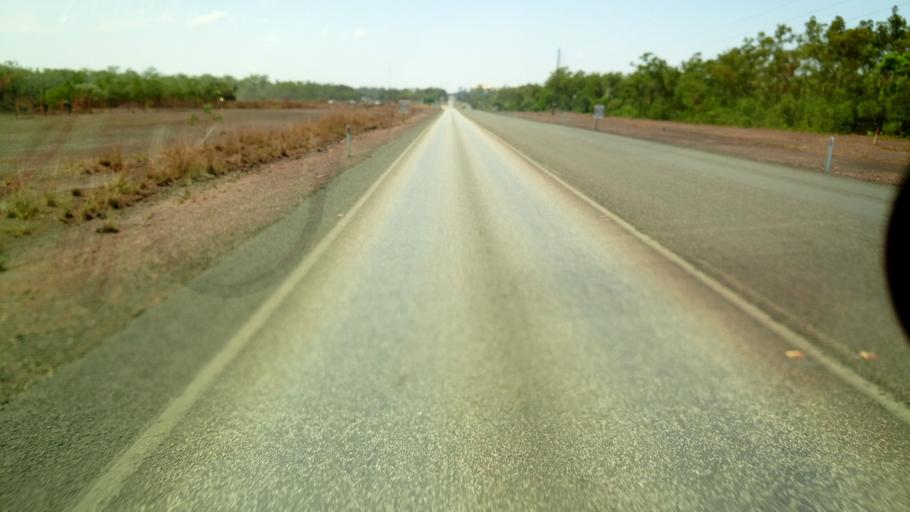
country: AU
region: Northern Territory
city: Alyangula
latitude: -13.9673
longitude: 136.4428
